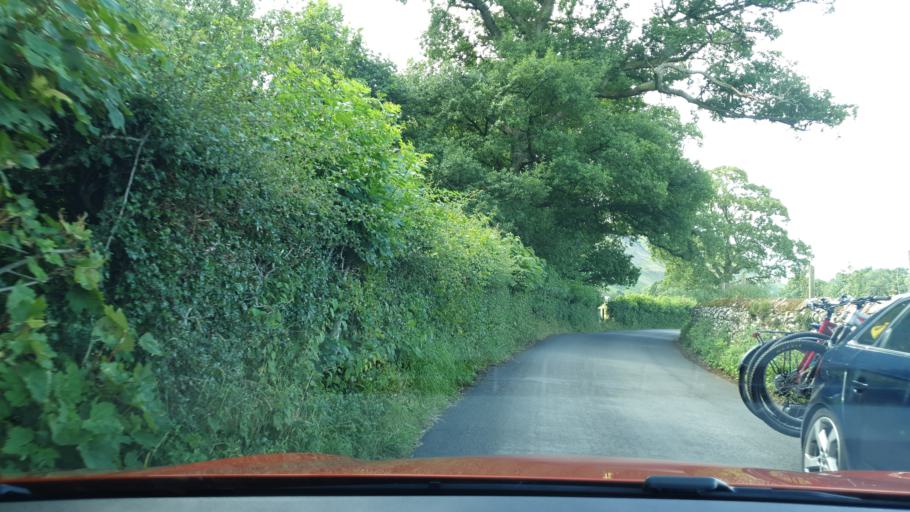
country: GB
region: England
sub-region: Cumbria
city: Penrith
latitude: 54.5934
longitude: -2.8400
